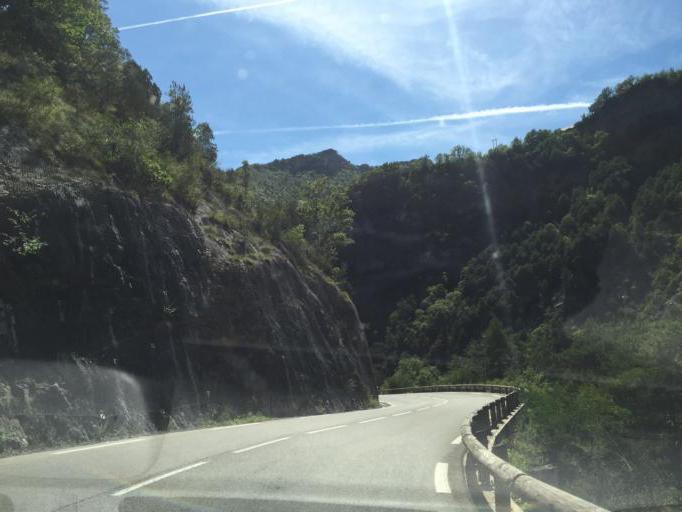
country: FR
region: Provence-Alpes-Cote d'Azur
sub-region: Departement des Alpes-Maritimes
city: Saint-Martin-Vesubie
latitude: 44.0401
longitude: 7.1283
